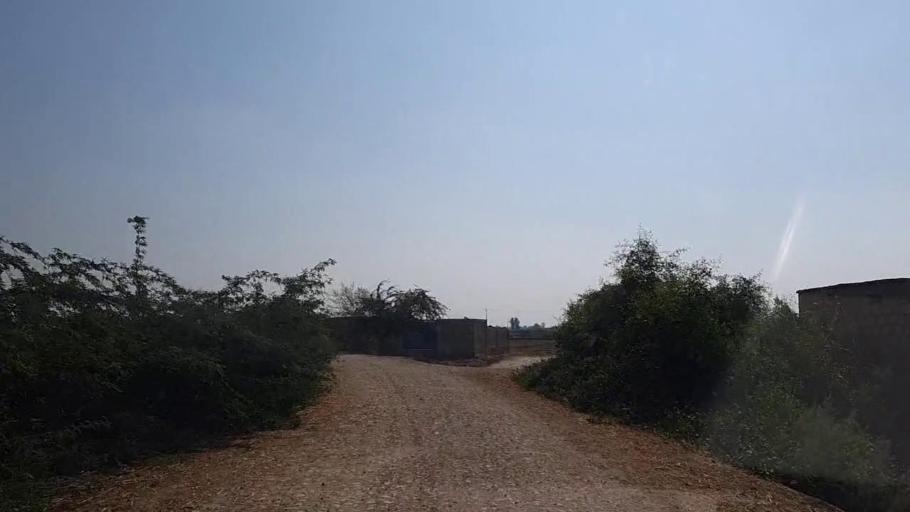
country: PK
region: Sindh
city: Thatta
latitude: 24.7678
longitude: 67.9421
